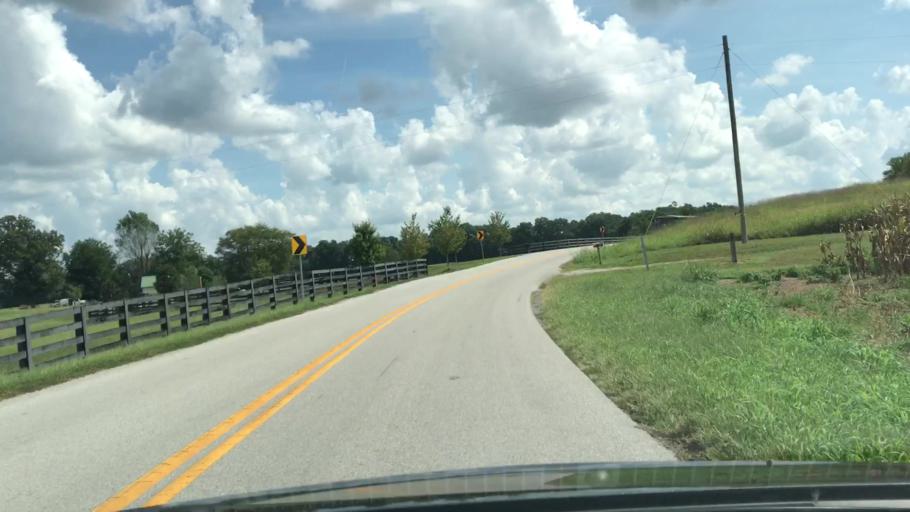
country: US
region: Tennessee
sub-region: Robertson County
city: Springfield
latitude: 36.6498
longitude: -86.9849
